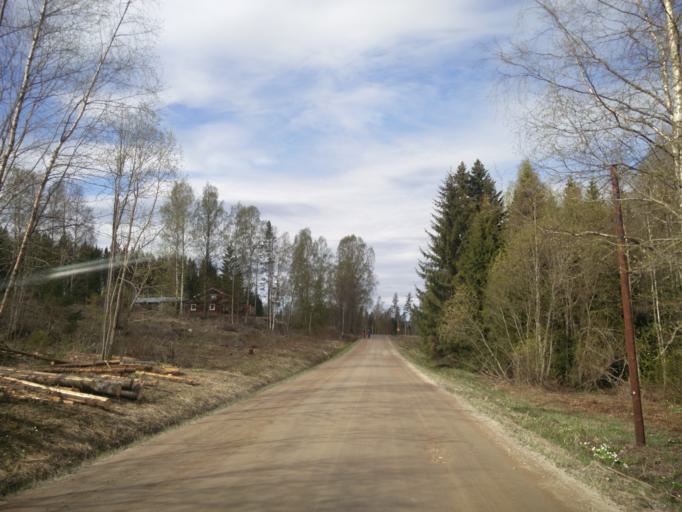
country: SE
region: Vaesternorrland
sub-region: Sundsvalls Kommun
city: Vi
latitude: 62.2706
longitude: 17.1844
